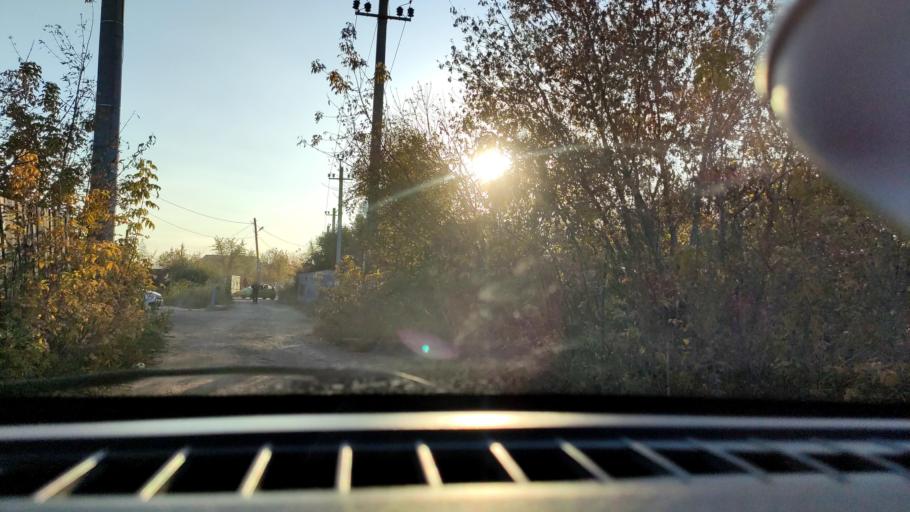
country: RU
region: Samara
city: Samara
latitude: 53.1823
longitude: 50.2245
